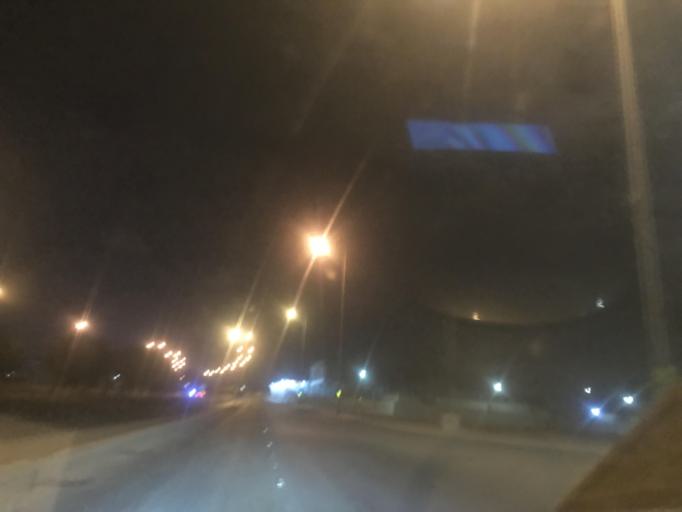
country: SA
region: Ar Riyad
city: Riyadh
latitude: 24.7863
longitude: 46.5907
